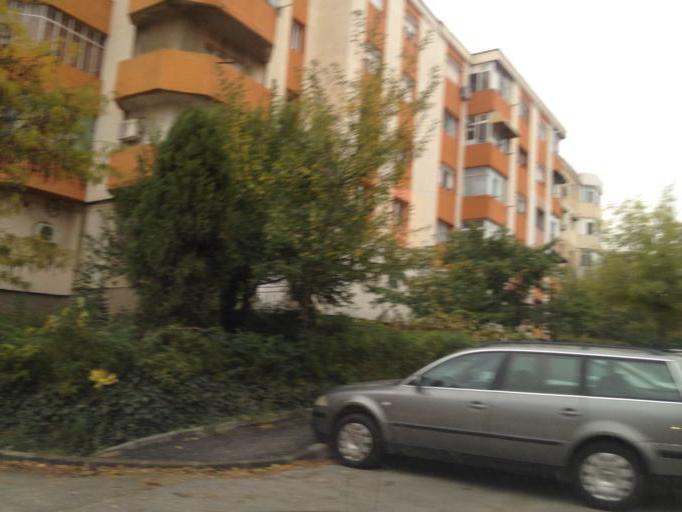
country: RO
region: Dolj
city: Craiova
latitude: 44.3323
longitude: 23.7906
